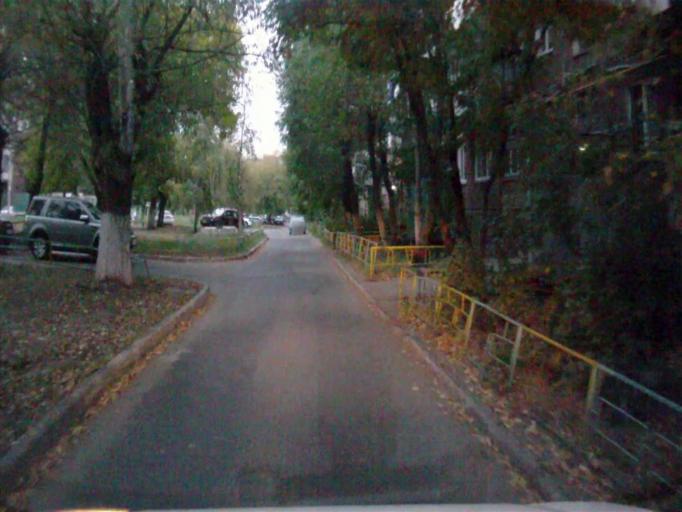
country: RU
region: Chelyabinsk
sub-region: Gorod Chelyabinsk
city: Chelyabinsk
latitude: 55.1896
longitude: 61.3361
